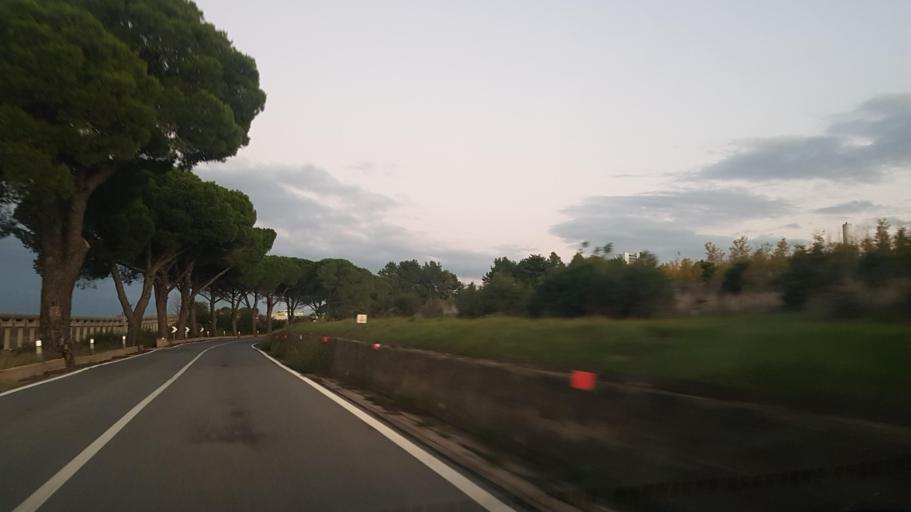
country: IT
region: Basilicate
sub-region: Provincia di Matera
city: Matera
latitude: 40.6794
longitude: 16.6484
